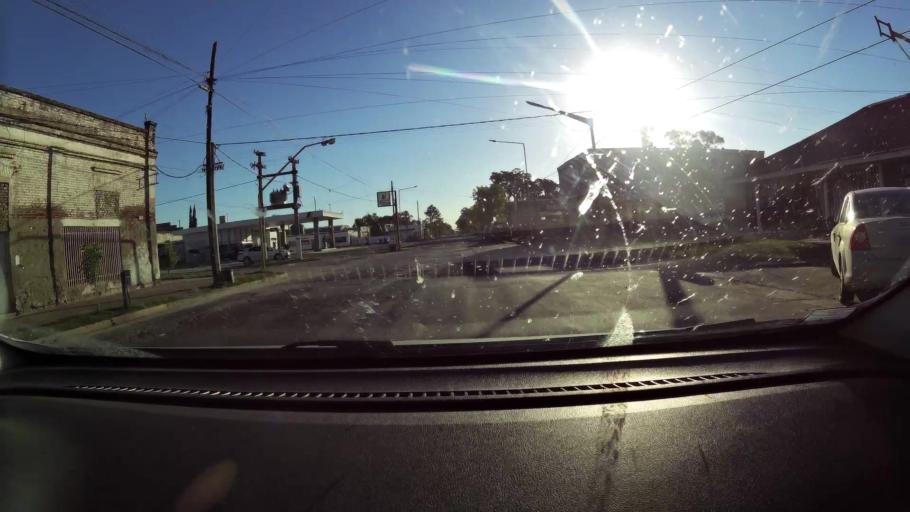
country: AR
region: Cordoba
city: Saturnino M. Laspiur
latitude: -31.7051
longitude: -62.4846
